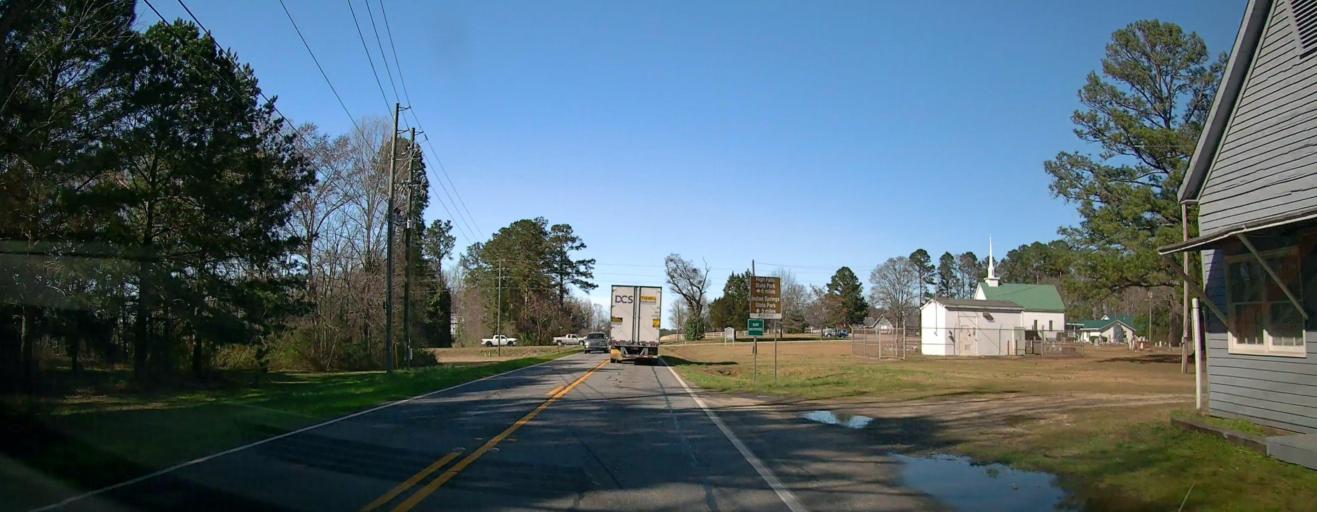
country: US
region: Georgia
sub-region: Butts County
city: Indian Springs
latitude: 33.1766
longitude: -83.9590
